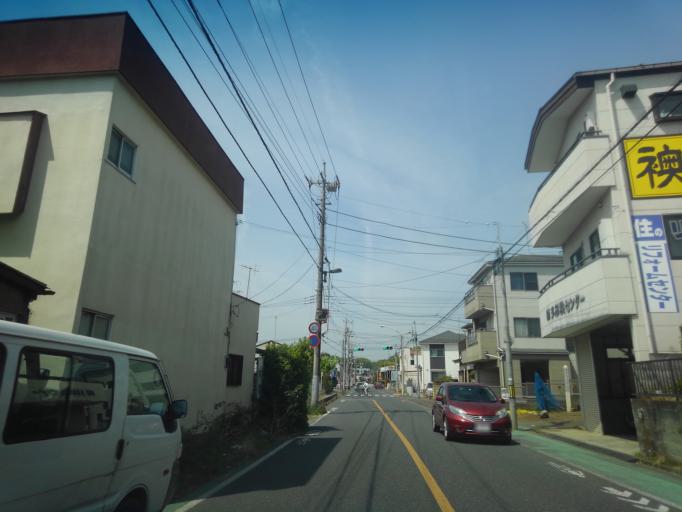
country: JP
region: Tokyo
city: Higashimurayama-shi
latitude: 35.7578
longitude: 139.4055
